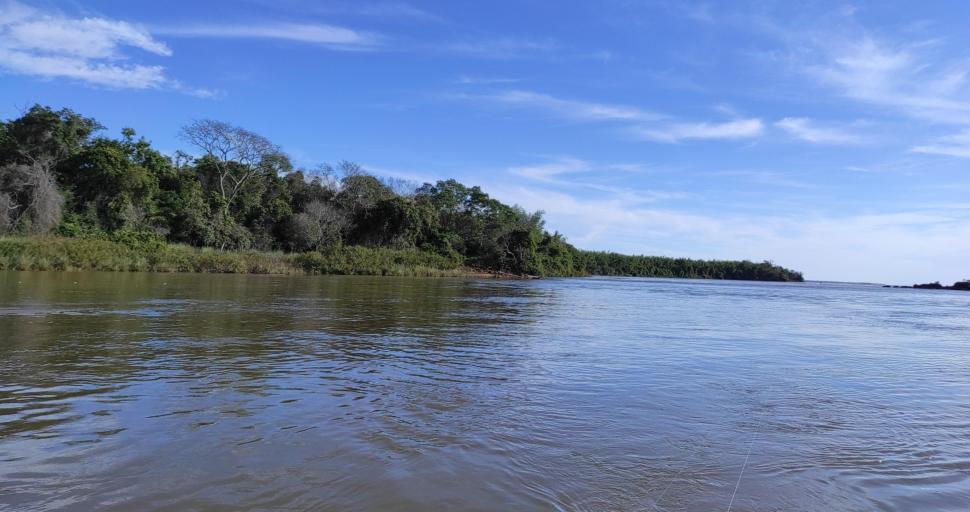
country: AR
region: Corrientes
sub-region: Departamento de Itati
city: Itati
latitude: -27.2790
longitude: -58.3178
